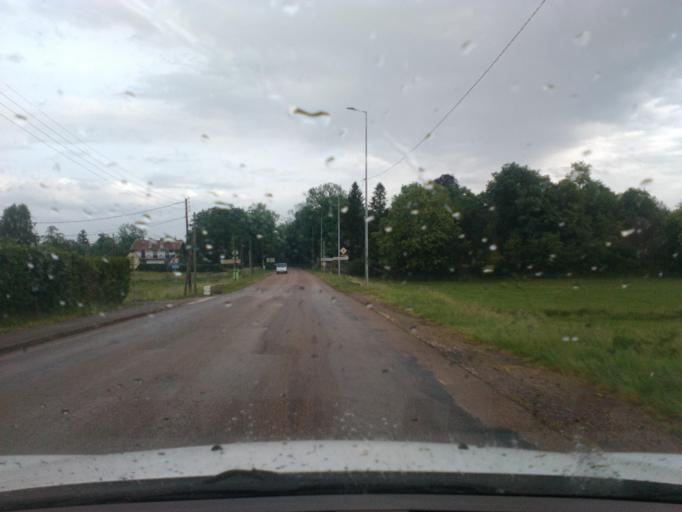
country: FR
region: Lorraine
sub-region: Departement des Vosges
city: Rambervillers
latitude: 48.3537
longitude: 6.6309
